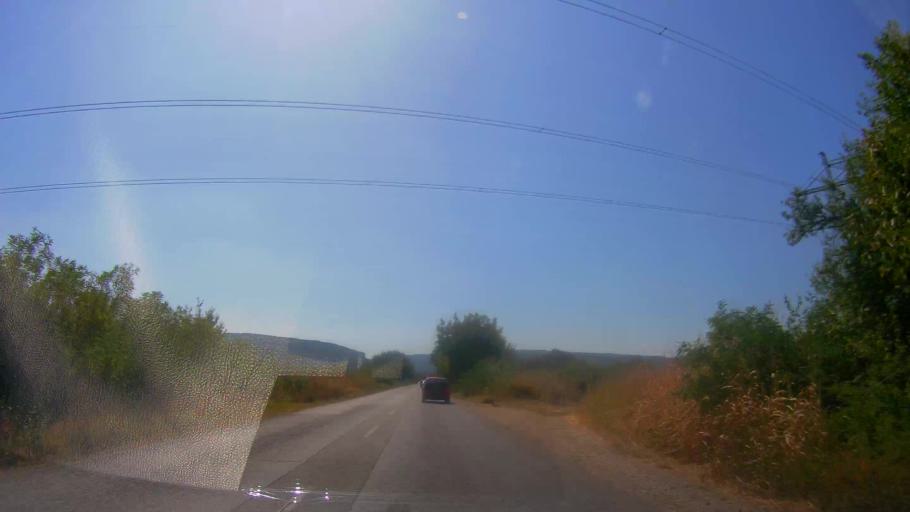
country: BG
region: Veliko Turnovo
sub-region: Obshtina Gorna Oryakhovitsa
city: Purvomaytsi
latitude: 43.1587
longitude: 25.6192
